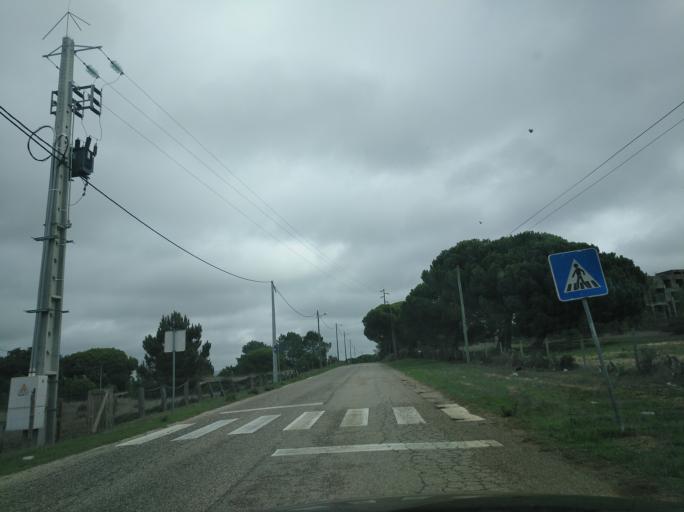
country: PT
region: Setubal
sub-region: Santiago do Cacem
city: Santo Andre
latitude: 38.1366
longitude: -8.7592
